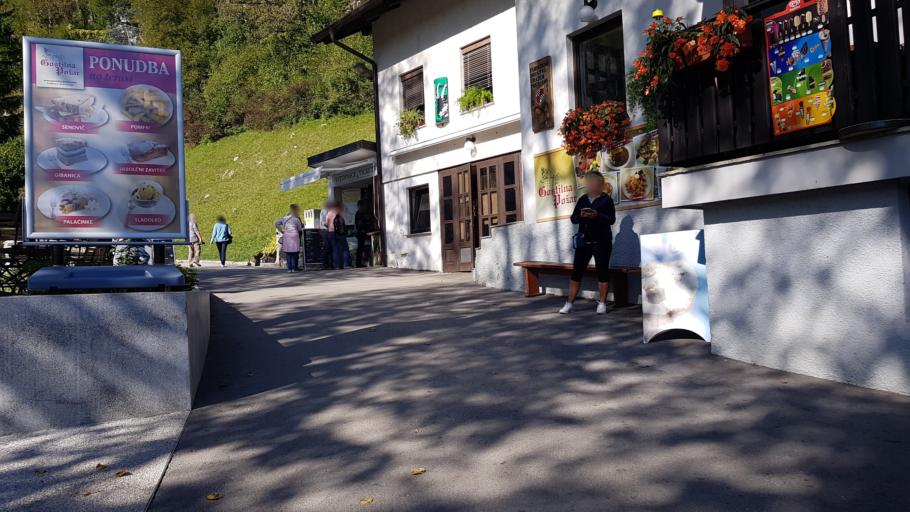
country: SI
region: Postojna
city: Postojna
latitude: 45.8149
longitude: 14.1279
